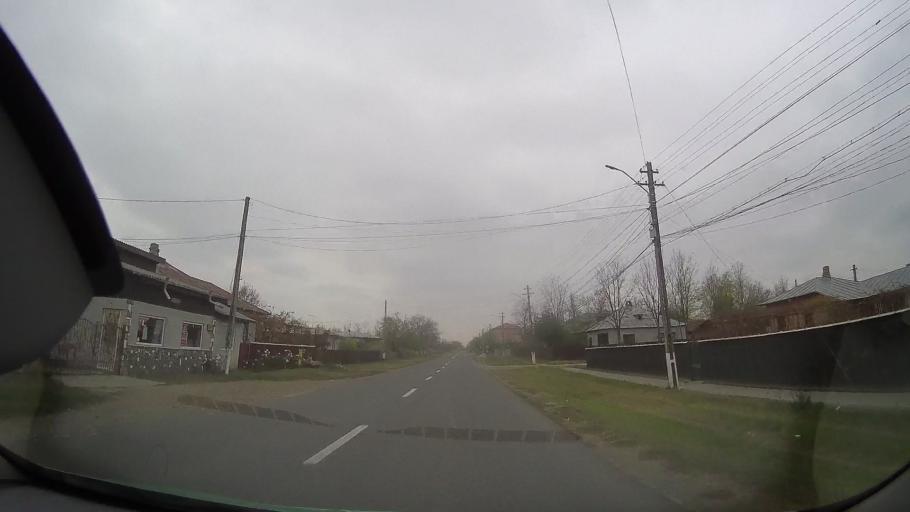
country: RO
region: Ialomita
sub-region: Comuna Garbovi
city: Garbovi
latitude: 44.7845
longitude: 26.7660
